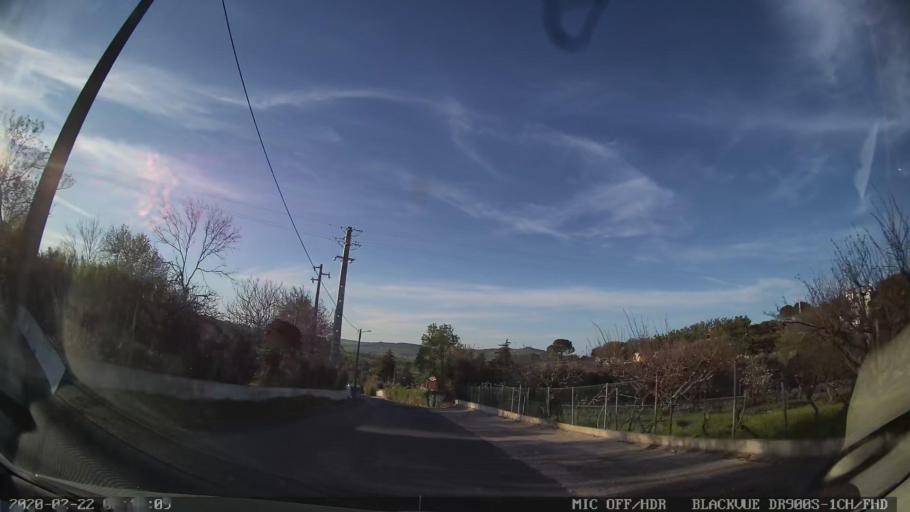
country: PT
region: Lisbon
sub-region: Vila Franca de Xira
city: Castanheira do Ribatejo
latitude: 38.9891
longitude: -9.0158
